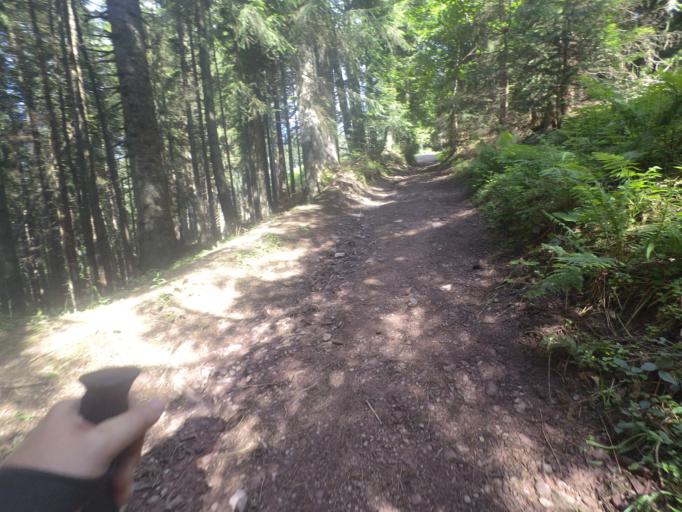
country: AT
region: Salzburg
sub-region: Politischer Bezirk Zell am See
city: Leogang
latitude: 47.4552
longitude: 12.7703
